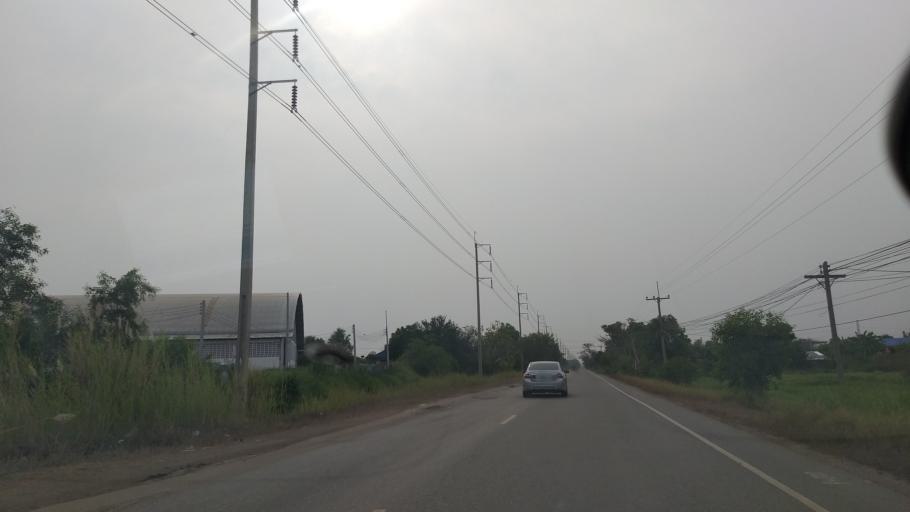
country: TH
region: Chachoengsao
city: Ban Pho
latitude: 13.5990
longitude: 101.1758
